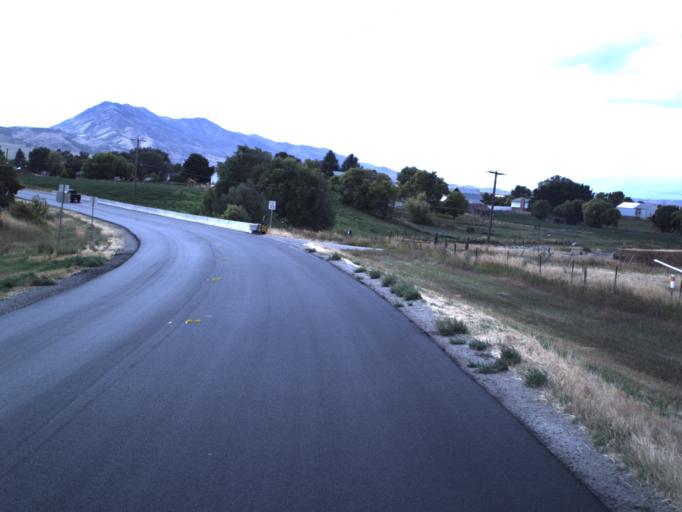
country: US
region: Utah
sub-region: Cache County
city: Benson
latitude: 41.8616
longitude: -111.9792
